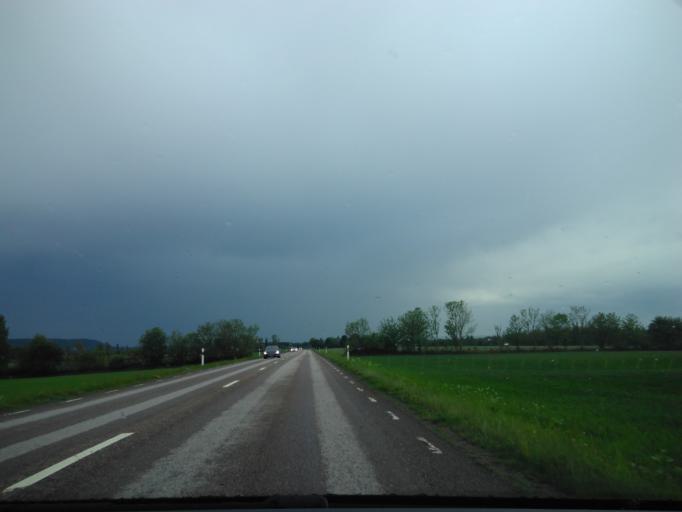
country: SE
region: Vaestra Goetaland
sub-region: Skovde Kommun
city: Skultorp
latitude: 58.2829
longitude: 13.7633
